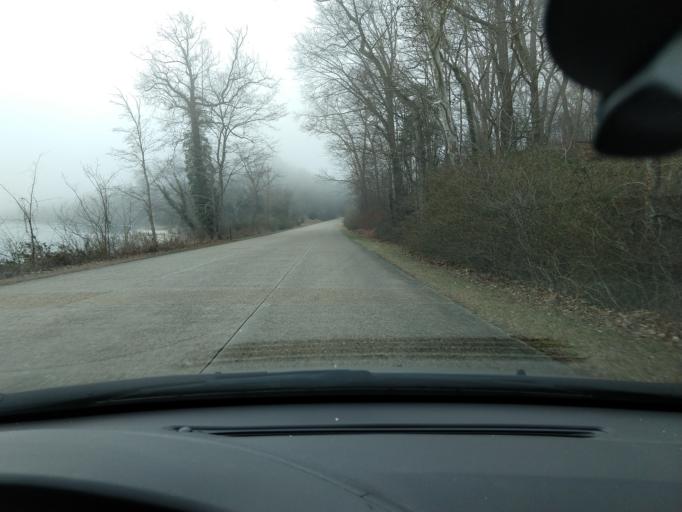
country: US
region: Virginia
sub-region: York County
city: Yorktown
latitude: 37.2435
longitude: -76.5267
